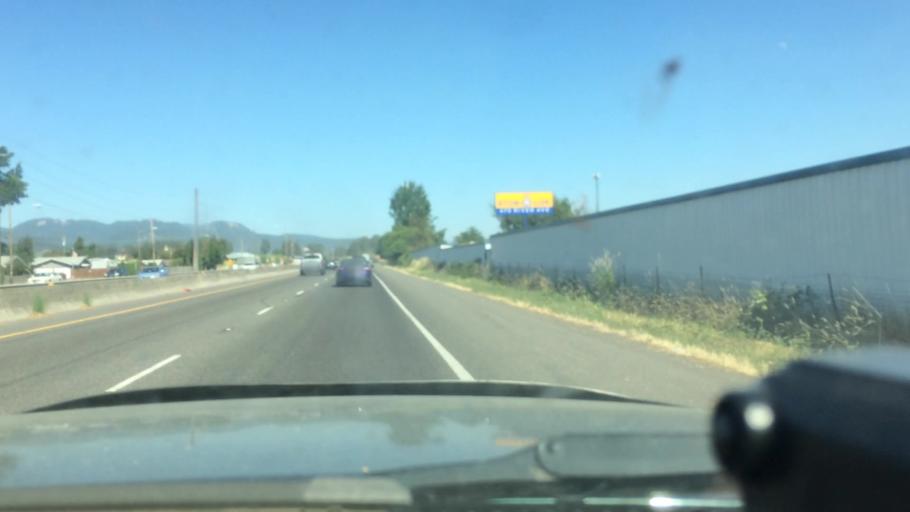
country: US
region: Oregon
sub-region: Lane County
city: Eugene
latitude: 44.0975
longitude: -123.1175
